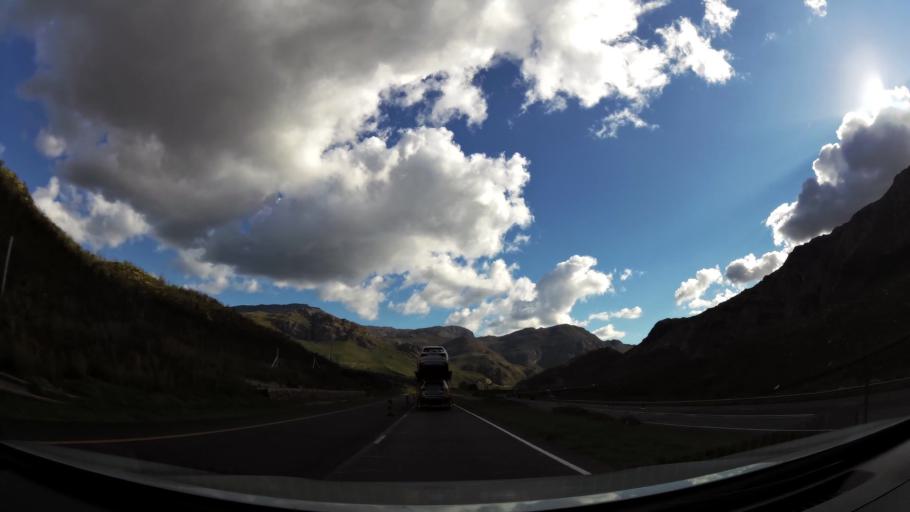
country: ZA
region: Western Cape
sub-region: Cape Winelands District Municipality
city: Paarl
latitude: -33.7258
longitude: 19.1421
